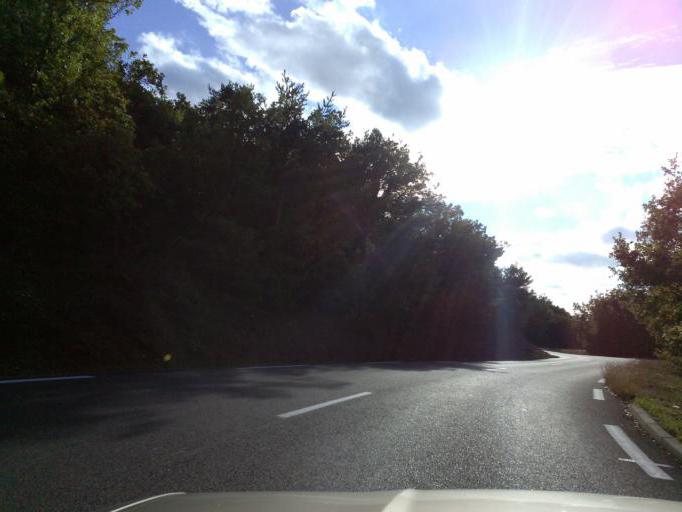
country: FR
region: Provence-Alpes-Cote d'Azur
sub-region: Departement des Alpes-de-Haute-Provence
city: Riez
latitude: 43.8995
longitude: 6.1381
